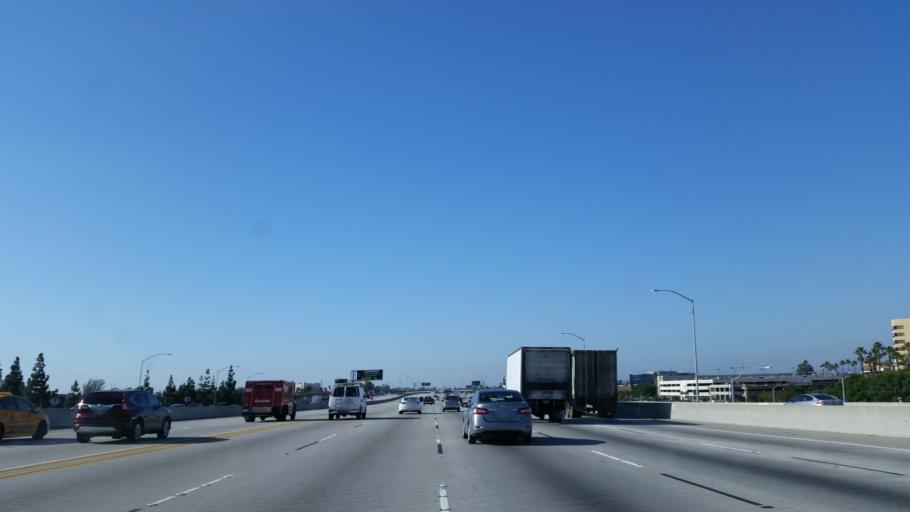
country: US
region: California
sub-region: Orange County
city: Orange
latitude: 33.7916
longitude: -117.8896
